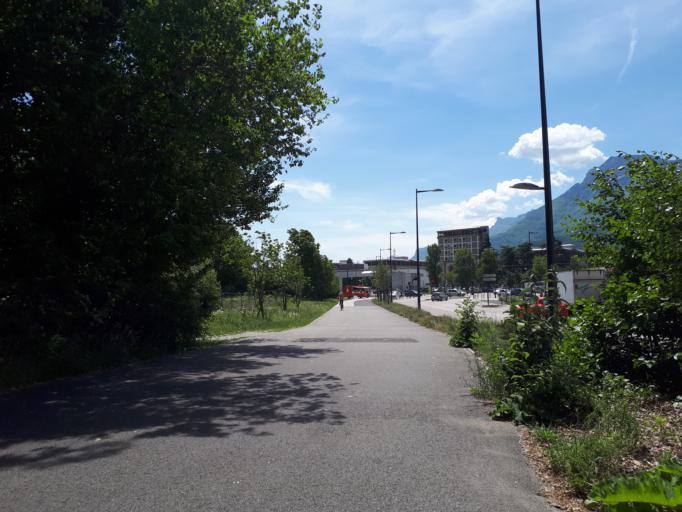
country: FR
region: Rhone-Alpes
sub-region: Departement de l'Isere
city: Saint-Martin-le-Vinoux
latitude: 45.2061
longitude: 5.7015
